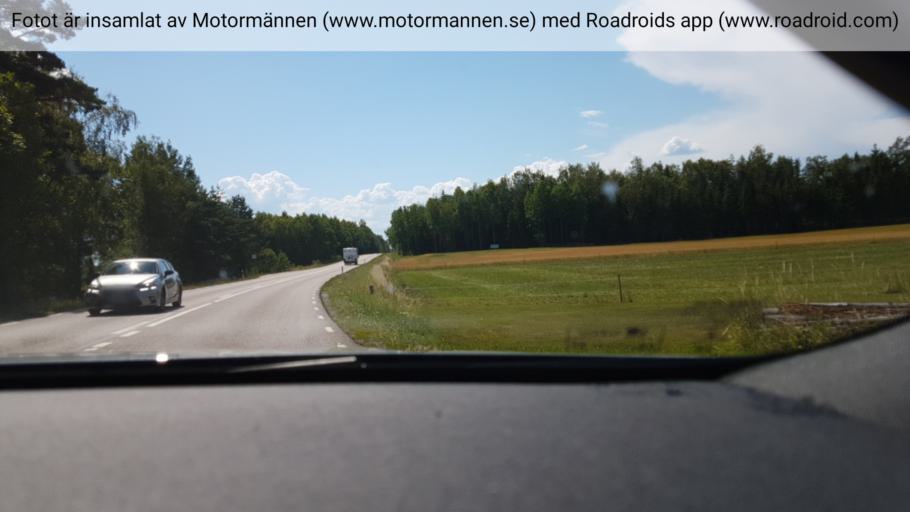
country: SE
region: Vaestra Goetaland
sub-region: Grastorps Kommun
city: Graestorp
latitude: 58.3880
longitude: 12.7618
